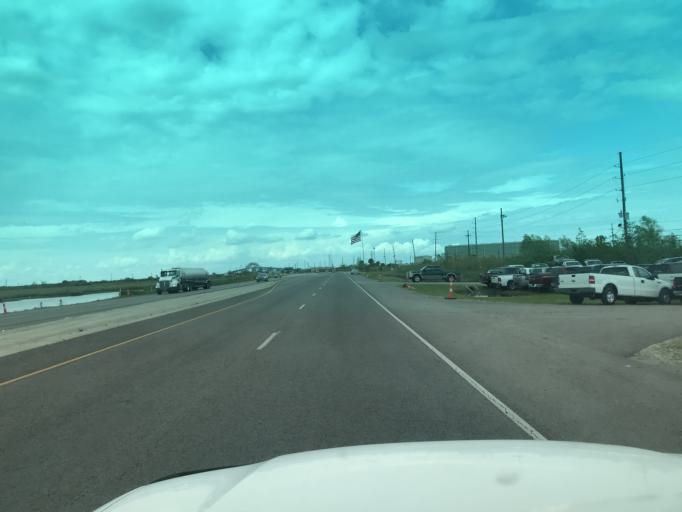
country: US
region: Louisiana
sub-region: Saint Bernard Parish
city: Chalmette
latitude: 29.9748
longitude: -89.9478
